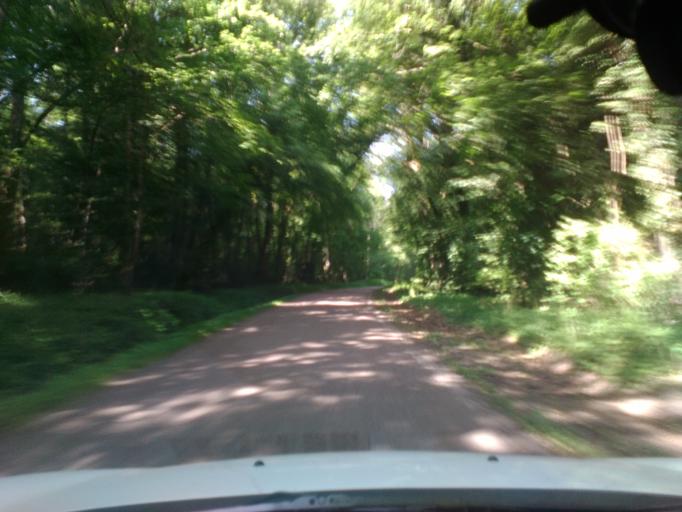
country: FR
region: Lorraine
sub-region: Departement des Vosges
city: Liffol-le-Grand
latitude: 48.2973
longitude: 5.4728
